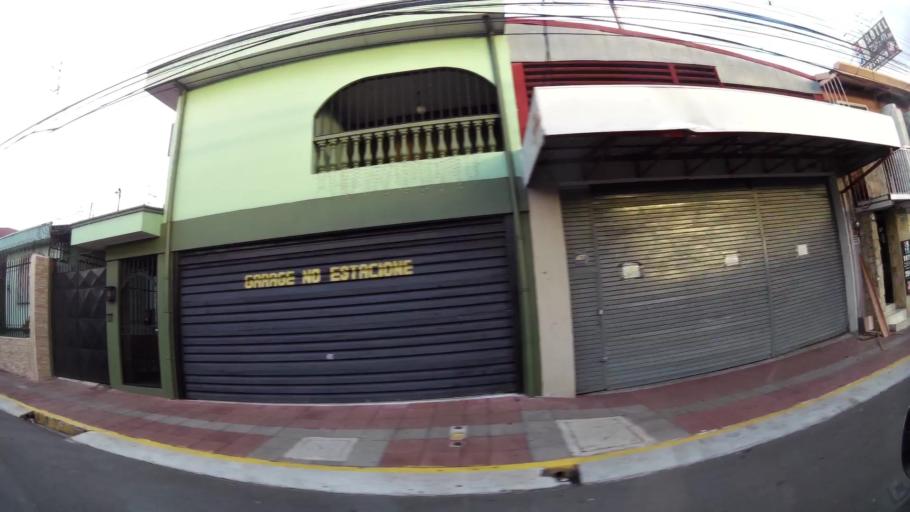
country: CR
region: Heredia
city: Heredia
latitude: 9.9963
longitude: -84.1218
